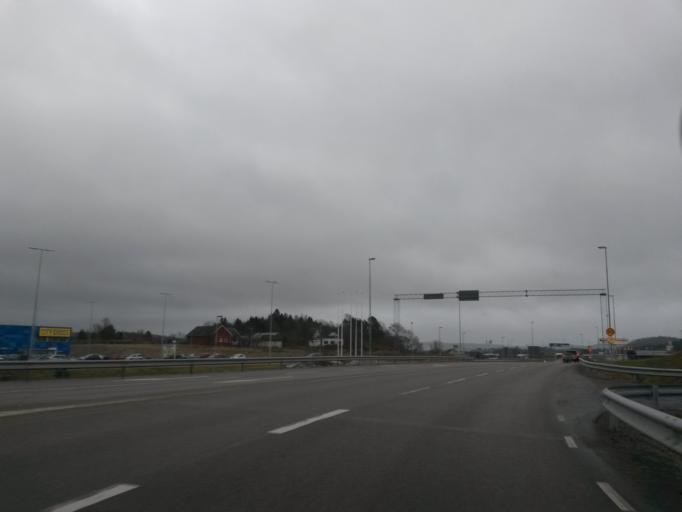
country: SE
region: Vaestra Goetaland
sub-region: Uddevalla Kommun
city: Uddevalla
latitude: 58.3523
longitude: 11.8225
